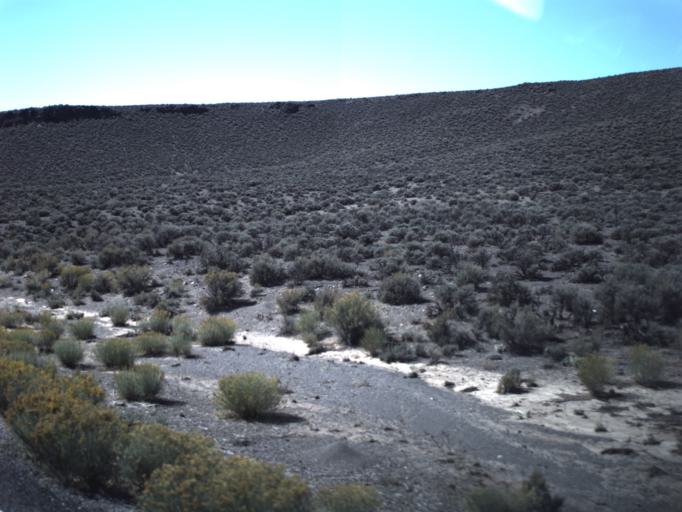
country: US
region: Utah
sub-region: Piute County
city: Junction
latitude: 38.1875
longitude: -112.0136
